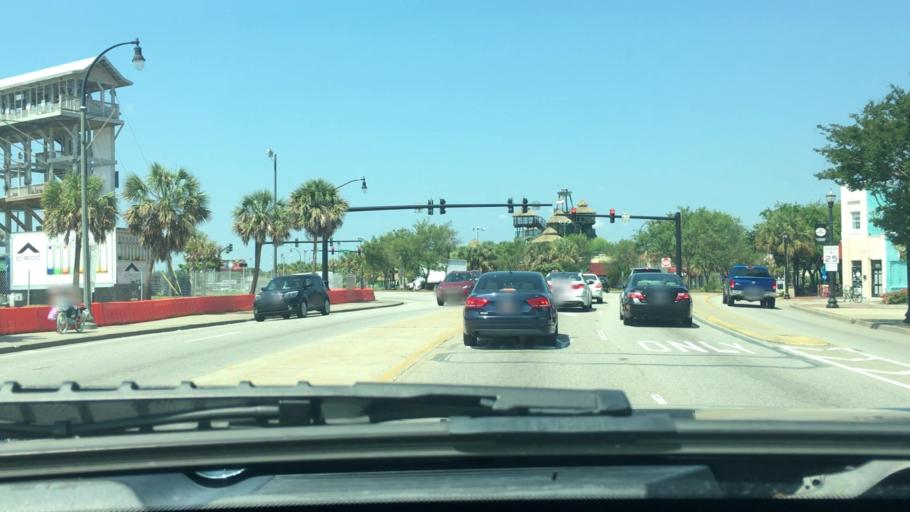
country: US
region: South Carolina
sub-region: Horry County
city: Myrtle Beach
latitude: 33.6935
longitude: -78.8827
